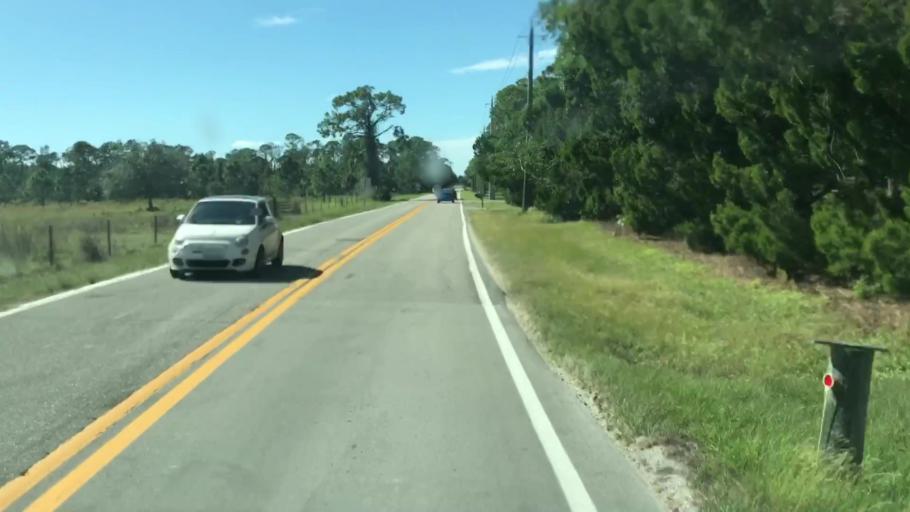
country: US
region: Florida
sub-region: Lee County
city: Olga
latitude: 26.7248
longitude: -81.6641
